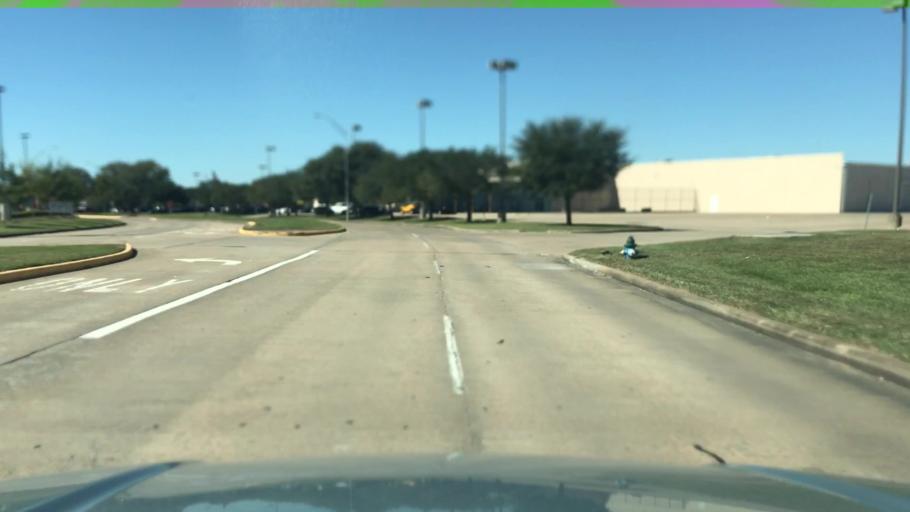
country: US
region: Texas
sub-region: Fort Bend County
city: Cinco Ranch
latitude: 29.7794
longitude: -95.7482
